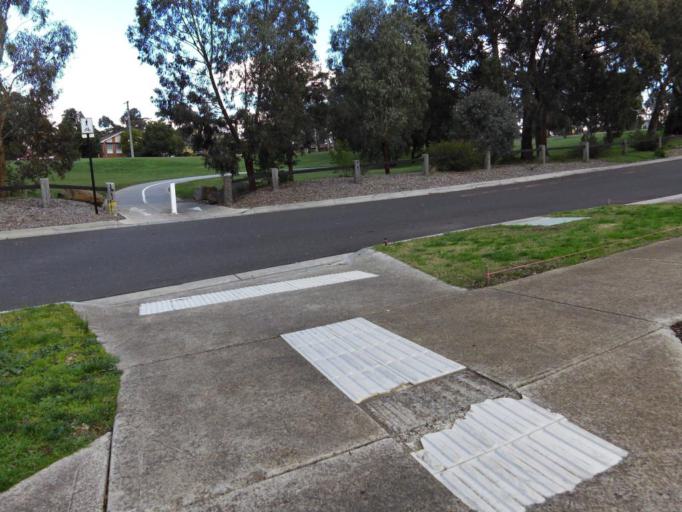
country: AU
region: Victoria
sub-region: Banyule
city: Watsonia North
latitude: -37.6880
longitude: 145.0881
